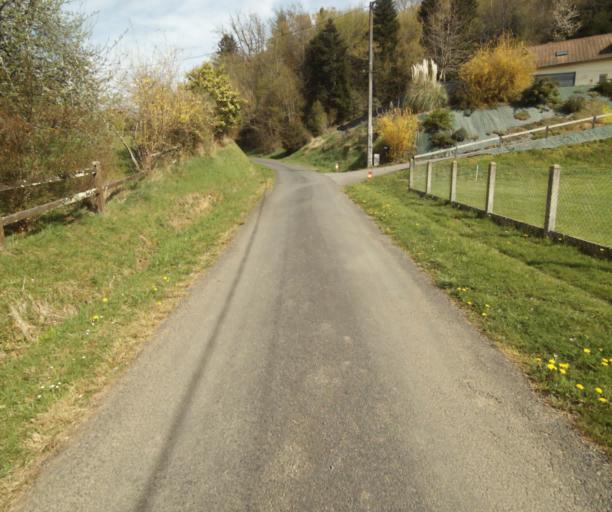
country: FR
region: Limousin
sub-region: Departement de la Correze
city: Laguenne
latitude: 45.2476
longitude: 1.8016
